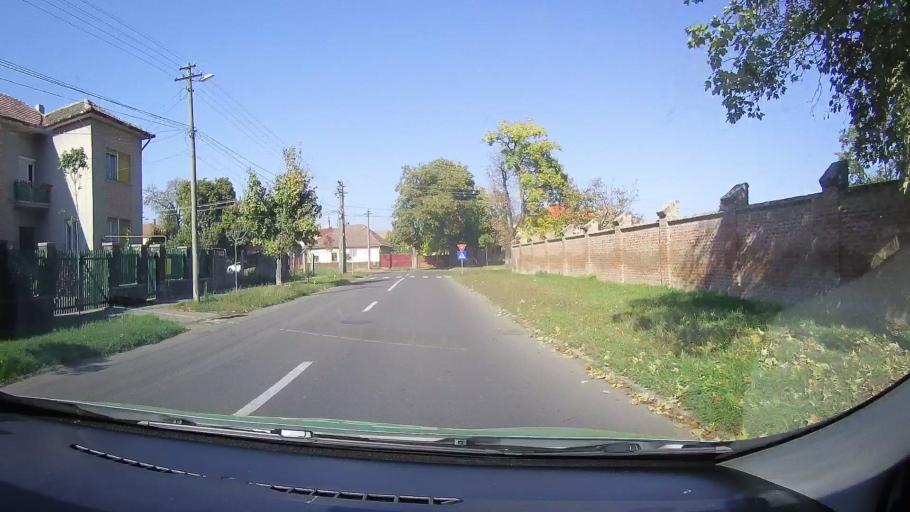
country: RO
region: Satu Mare
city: Carei
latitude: 47.6829
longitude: 22.4632
